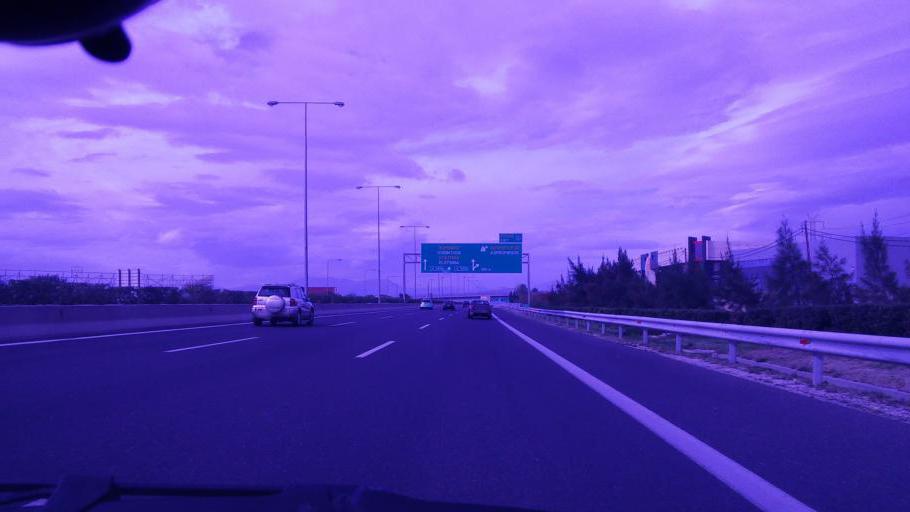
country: GR
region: Attica
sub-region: Nomarchia Dytikis Attikis
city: Fyli
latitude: 38.0878
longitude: 23.6317
